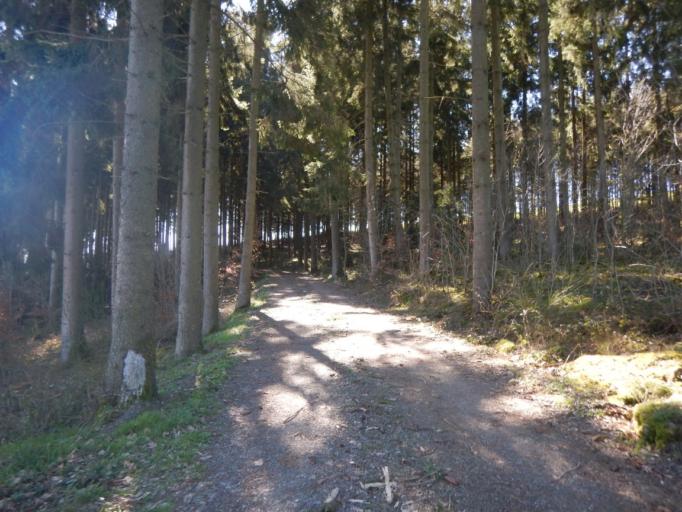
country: LU
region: Diekirch
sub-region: Canton de Wiltz
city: Eschweiler
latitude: 49.9986
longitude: 5.9251
